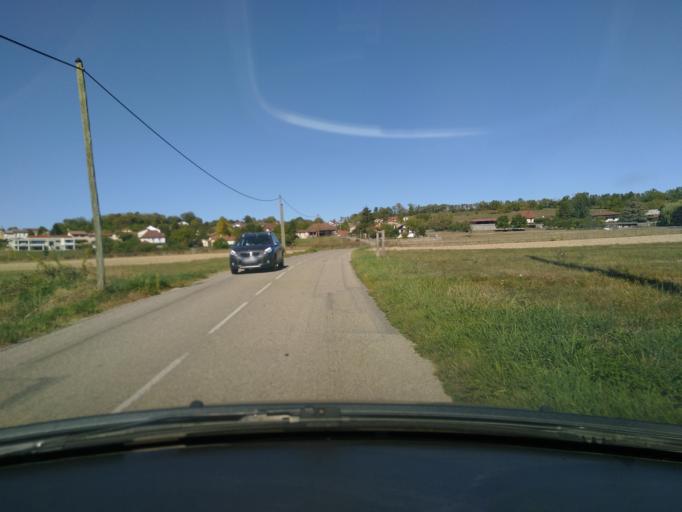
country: FR
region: Rhone-Alpes
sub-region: Departement de l'Isere
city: La Murette
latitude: 45.3754
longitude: 5.5233
